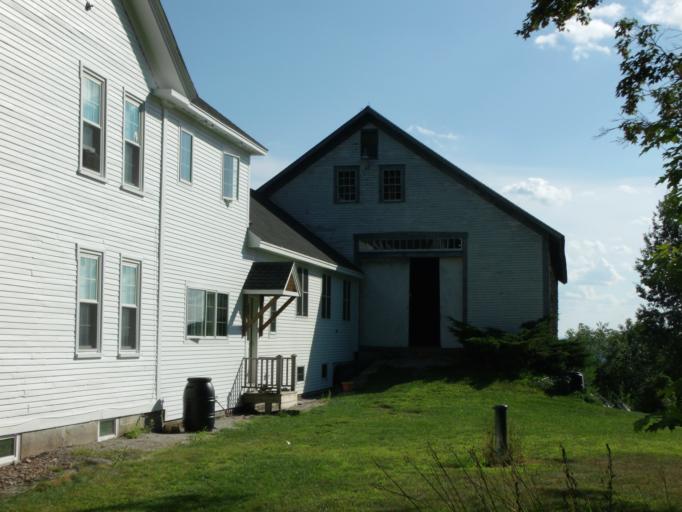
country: US
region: New Hampshire
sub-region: Merrimack County
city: Canterbury
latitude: 43.3298
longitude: -71.5577
